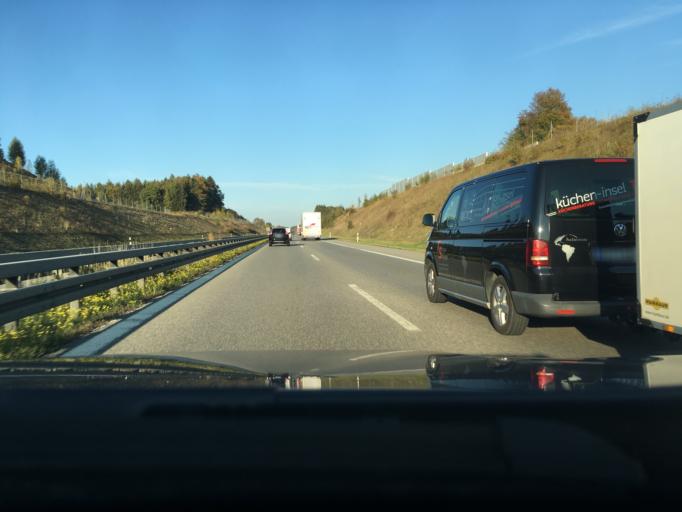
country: DE
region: Baden-Wuerttemberg
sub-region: Tuebingen Region
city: Kisslegg
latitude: 47.7597
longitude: 9.9134
